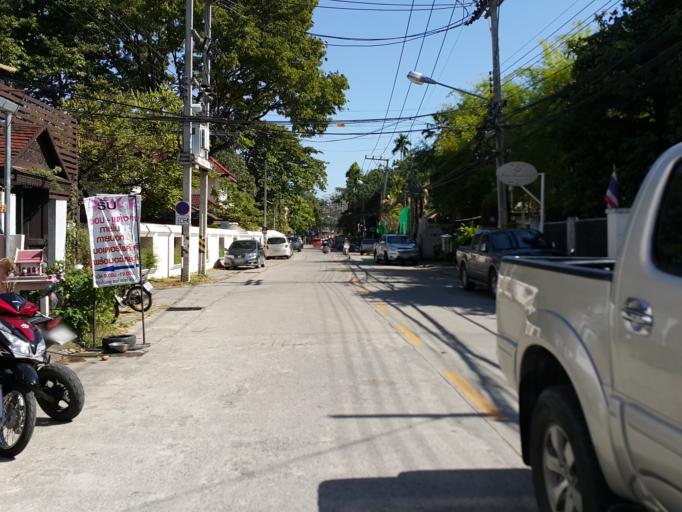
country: TH
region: Chiang Mai
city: Chiang Mai
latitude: 18.7931
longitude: 98.9857
